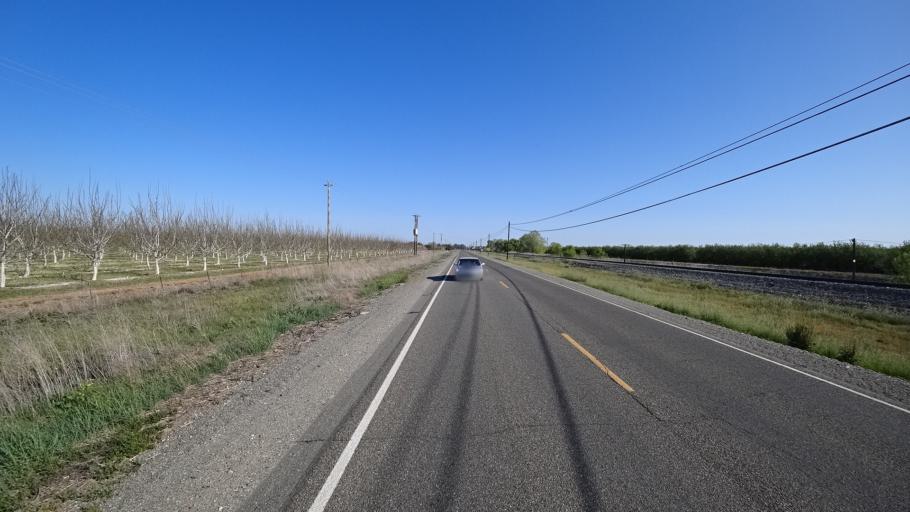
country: US
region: California
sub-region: Glenn County
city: Willows
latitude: 39.5653
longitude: -122.1938
